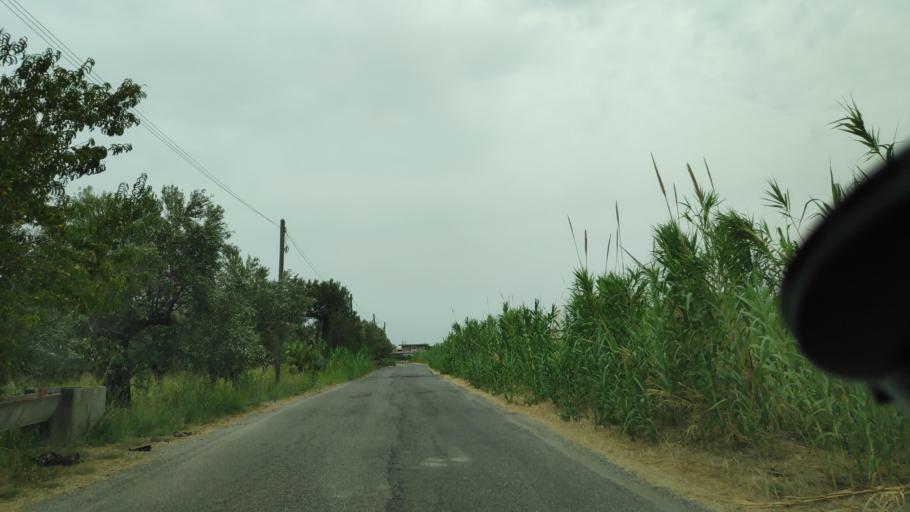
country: IT
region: Calabria
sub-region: Provincia di Catanzaro
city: Marina di Davoli
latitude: 38.6626
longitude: 16.5341
